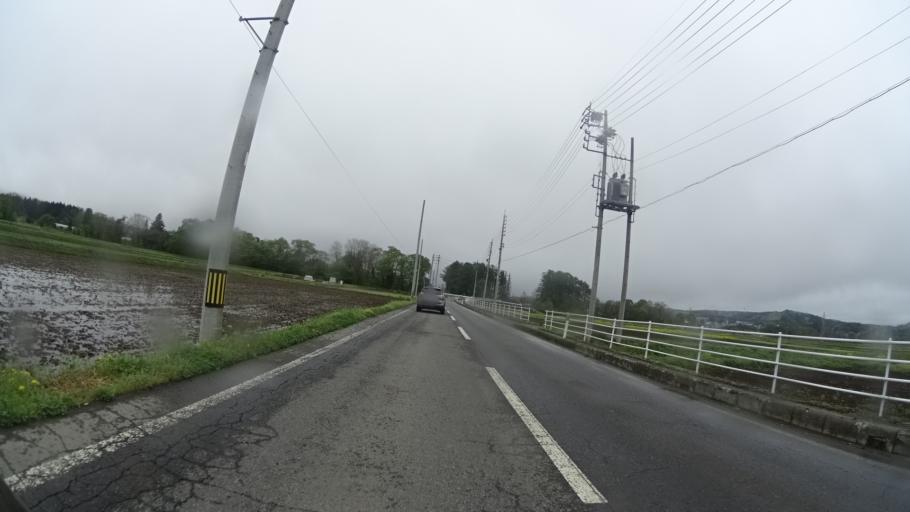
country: JP
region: Nagano
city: Nagano-shi
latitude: 36.7916
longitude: 138.1961
